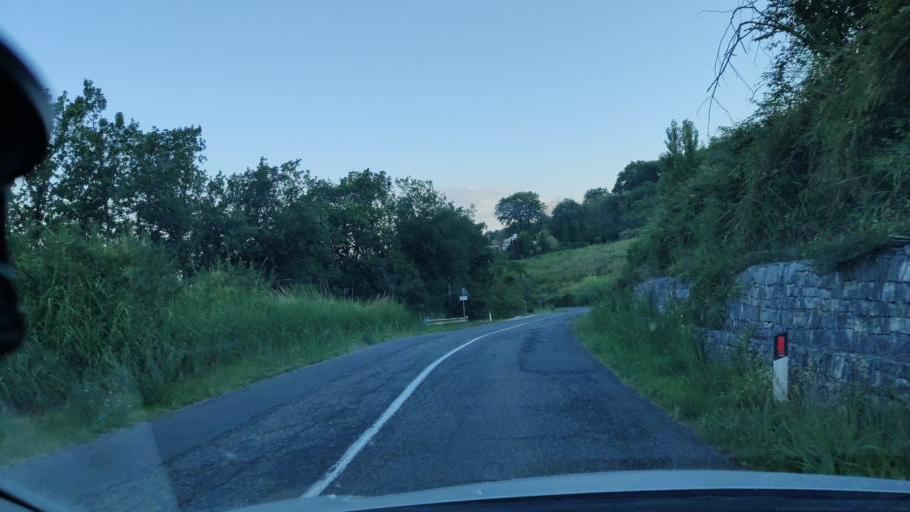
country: IT
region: Umbria
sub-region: Provincia di Terni
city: Giove
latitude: 42.5050
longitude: 12.3227
